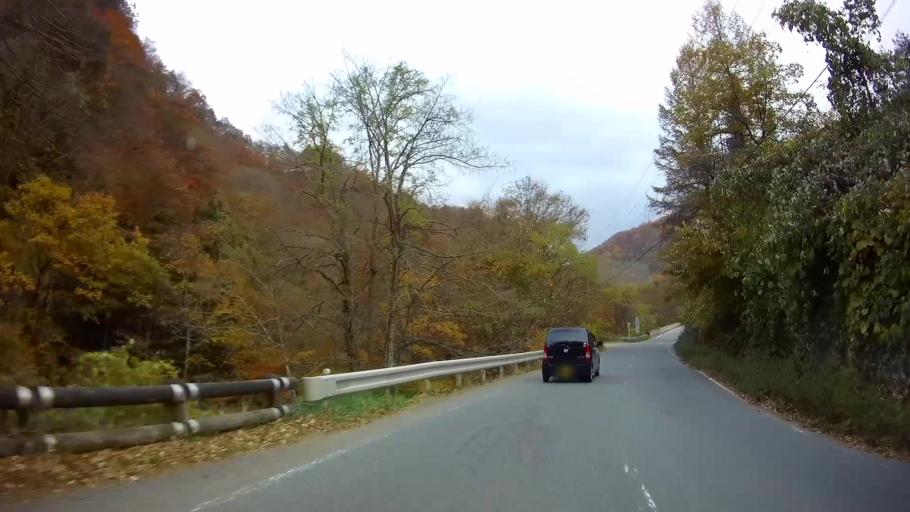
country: JP
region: Gunma
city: Nakanojomachi
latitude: 36.6341
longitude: 138.6544
